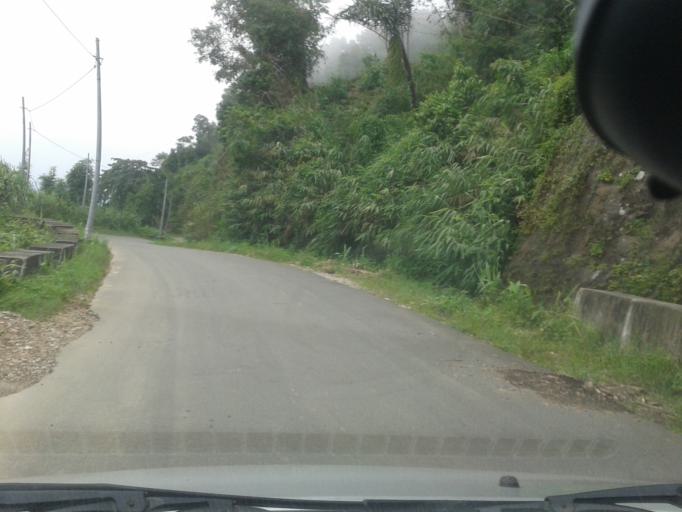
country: IN
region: Meghalaya
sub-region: East Khasi Hills
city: Cherrapunji
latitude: 25.2068
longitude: 91.7401
